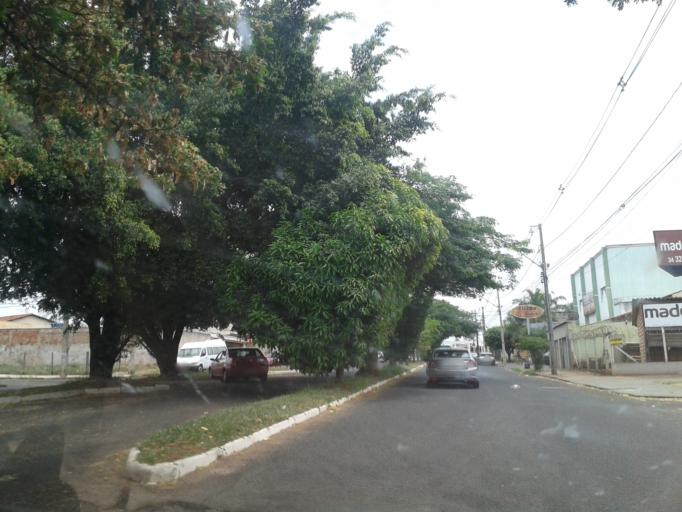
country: BR
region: Minas Gerais
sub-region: Uberlandia
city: Uberlandia
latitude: -18.9119
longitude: -48.3166
